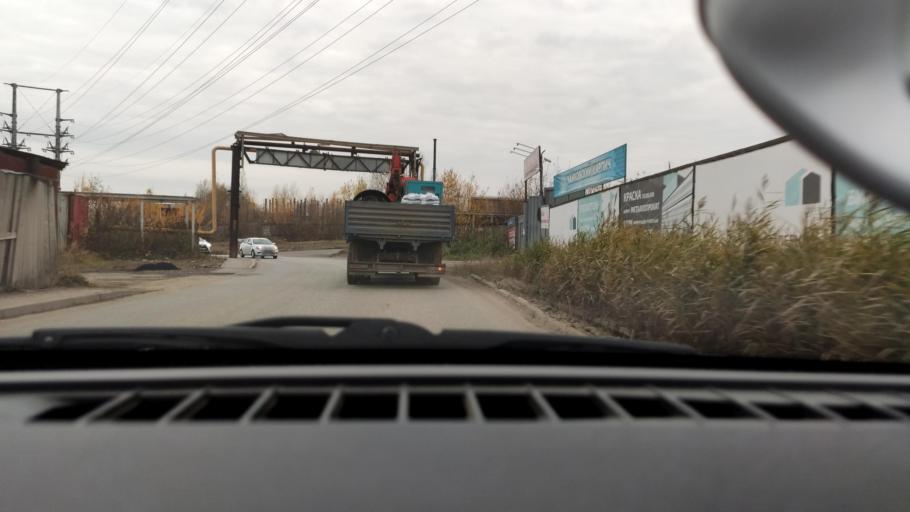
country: RU
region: Perm
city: Kondratovo
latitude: 58.0032
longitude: 56.1403
